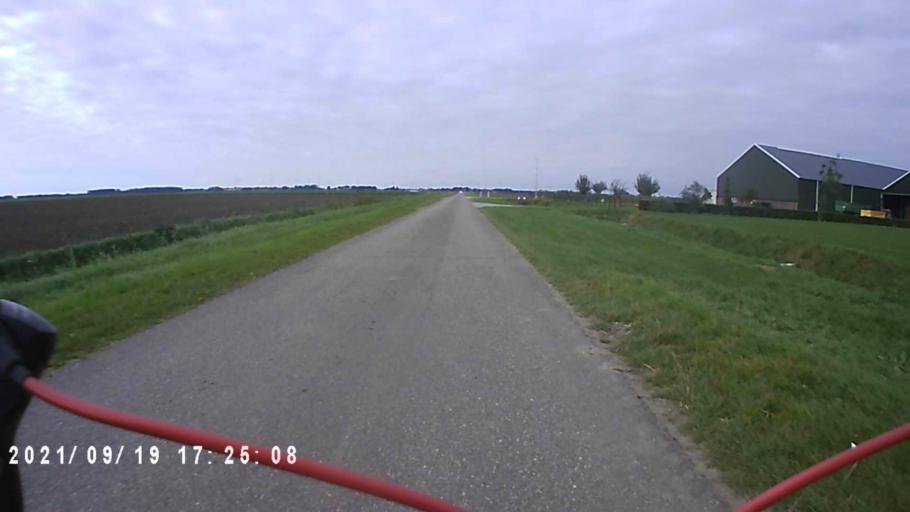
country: NL
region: Groningen
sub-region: Gemeente  Oldambt
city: Winschoten
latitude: 53.2208
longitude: 7.0136
